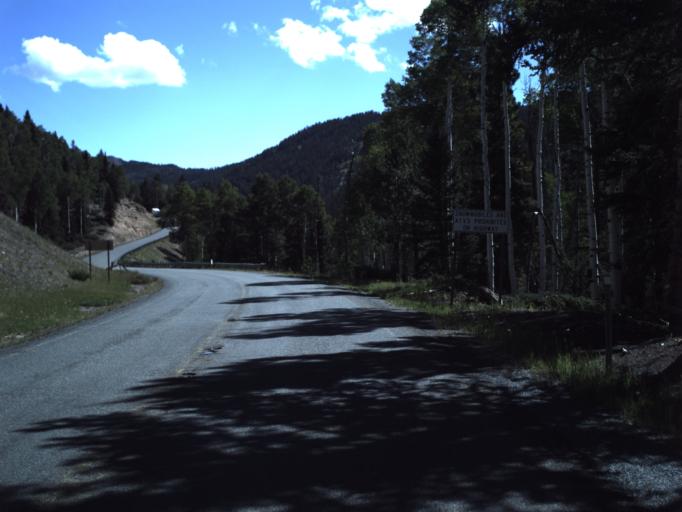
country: US
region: Utah
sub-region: Piute County
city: Junction
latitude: 38.3067
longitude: -112.4091
